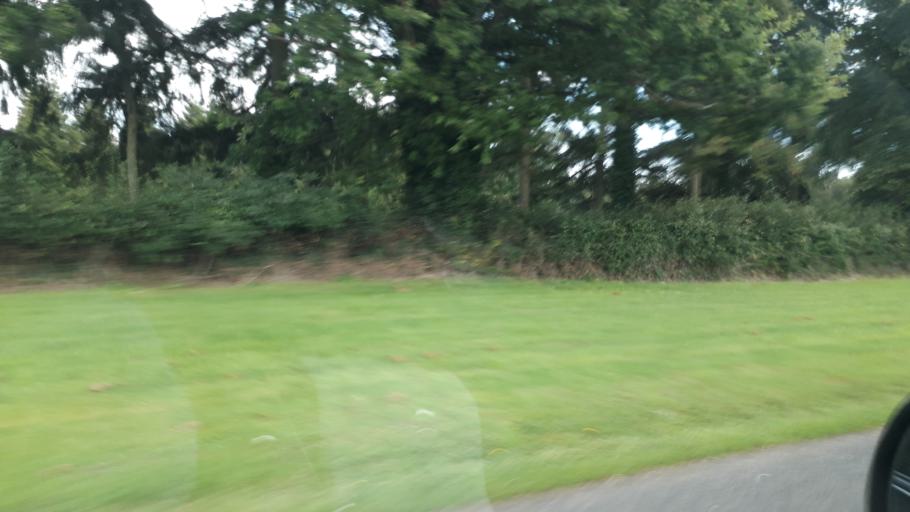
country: IE
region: Leinster
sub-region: Lu
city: Blackrock
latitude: 54.0308
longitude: -6.3553
